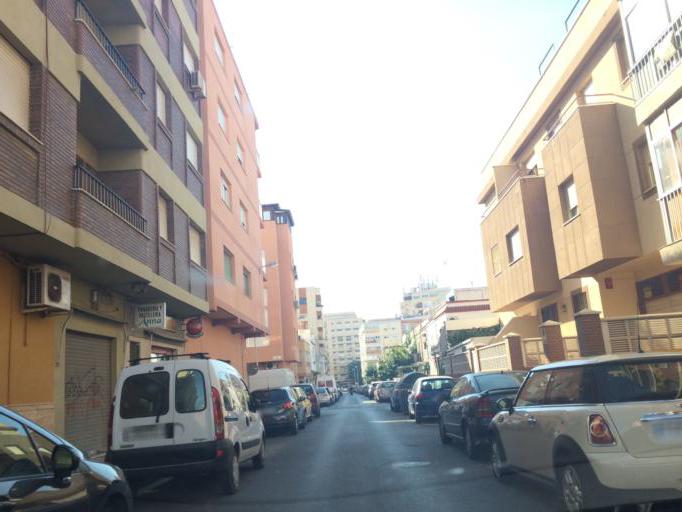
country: ES
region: Andalusia
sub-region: Provincia de Almeria
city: Almeria
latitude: 36.8299
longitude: -2.4497
